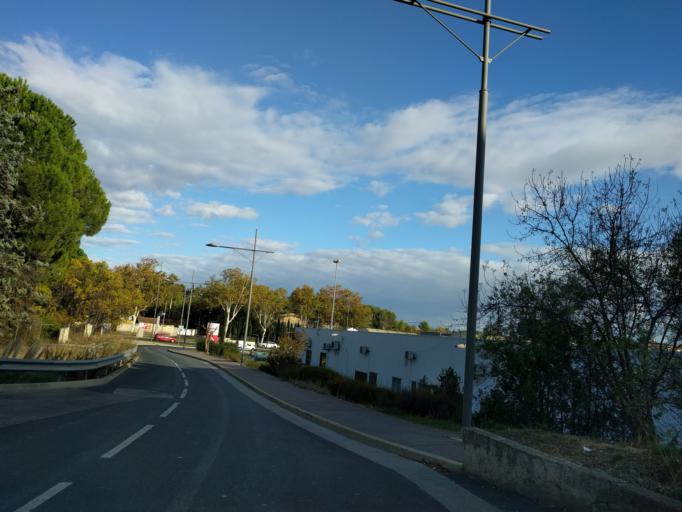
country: FR
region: Languedoc-Roussillon
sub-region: Departement de l'Herault
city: Montferrier-sur-Lez
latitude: 43.6420
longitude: 3.8446
